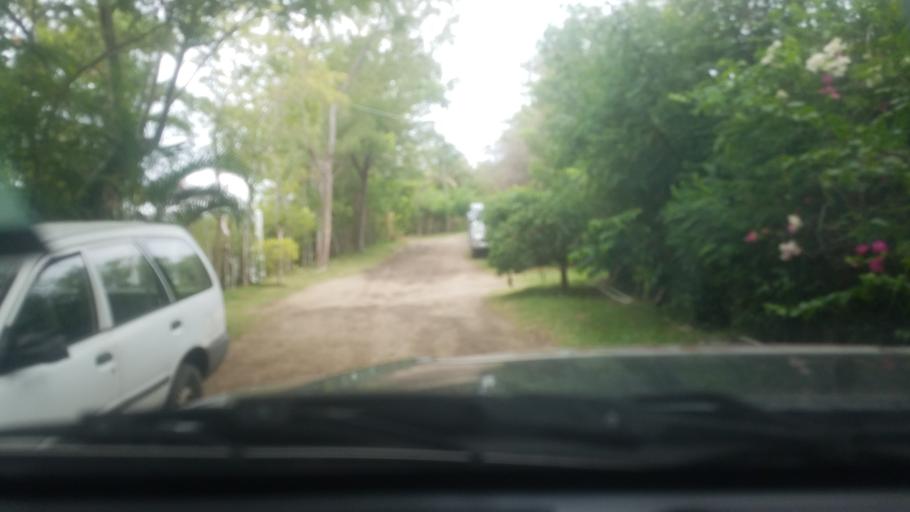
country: LC
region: Laborie Quarter
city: Laborie
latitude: 13.7485
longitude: -60.9784
